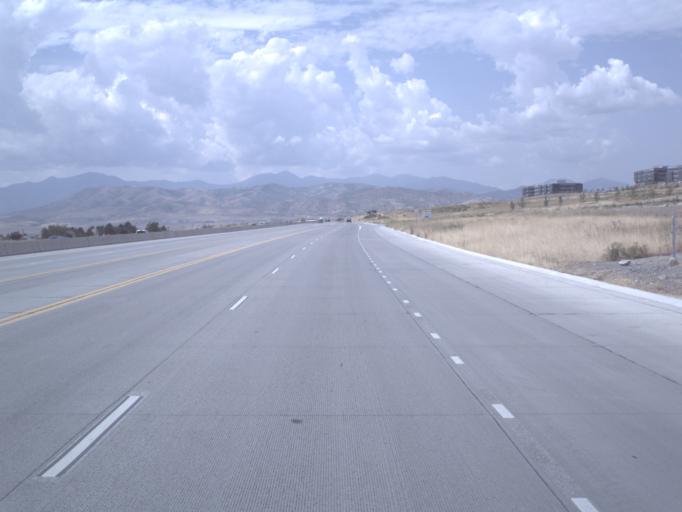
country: US
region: Utah
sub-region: Utah County
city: Lehi
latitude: 40.4326
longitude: -111.8580
